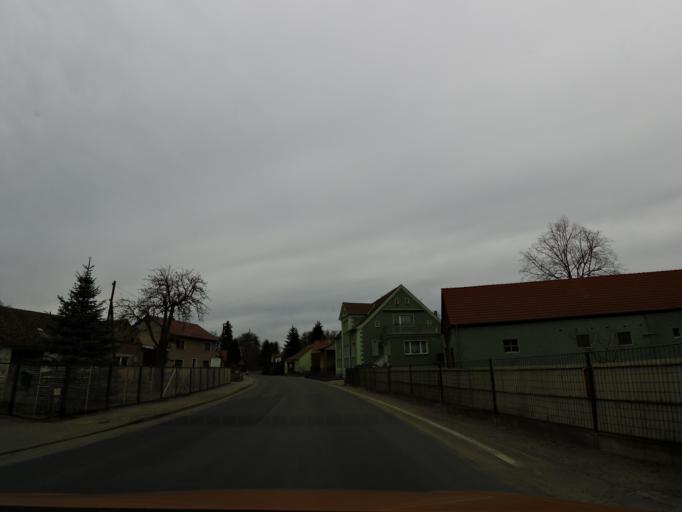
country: DE
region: Brandenburg
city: Bruck
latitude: 52.1694
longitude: 12.7358
